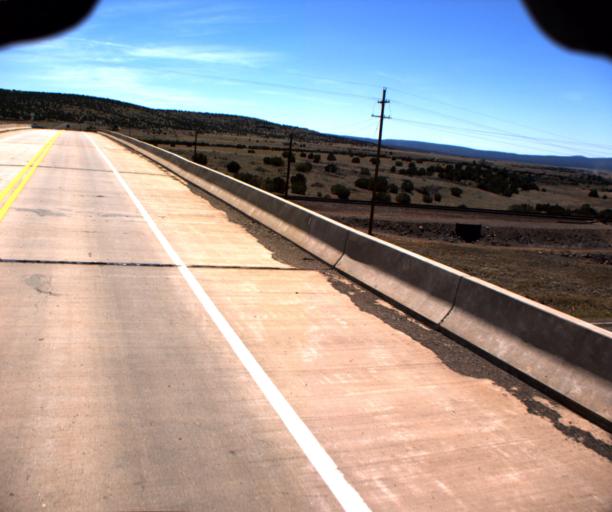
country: US
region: Arizona
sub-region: Mohave County
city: Peach Springs
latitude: 35.3298
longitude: -112.8902
